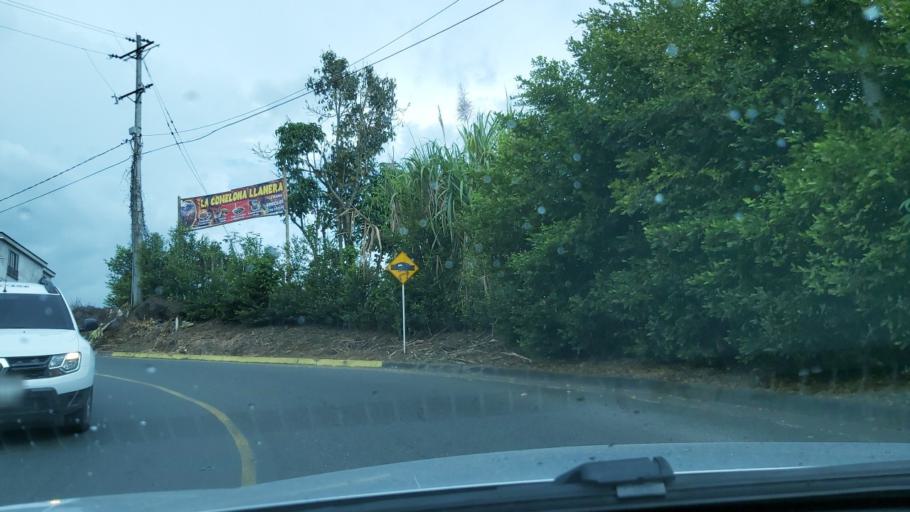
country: CO
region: Risaralda
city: Pereira
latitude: 4.7951
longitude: -75.7095
